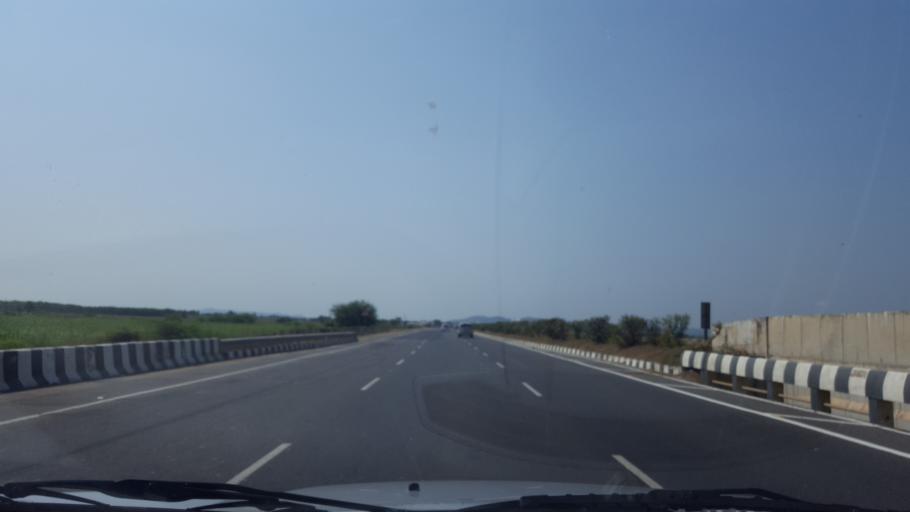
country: IN
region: Andhra Pradesh
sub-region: Guntur
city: Chilakalurupet
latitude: 16.0213
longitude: 80.1240
